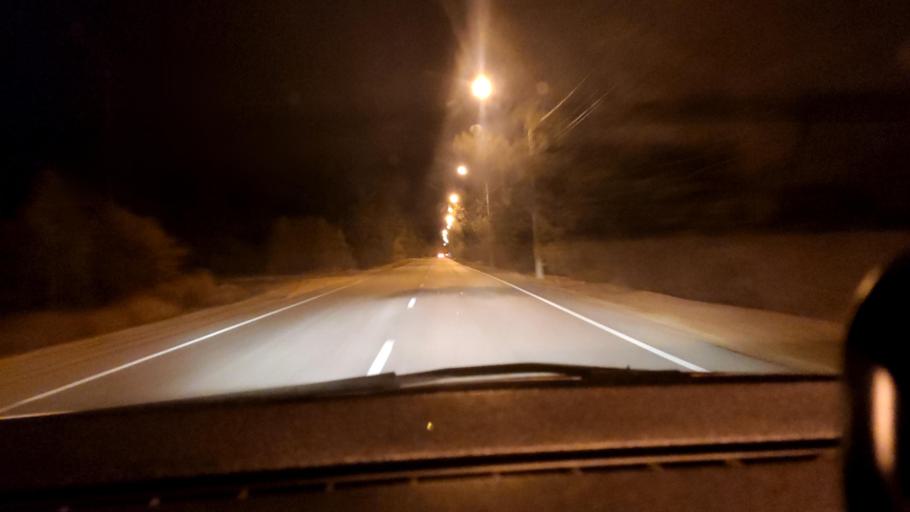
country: RU
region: Voronezj
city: Shilovo
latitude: 51.6088
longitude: 39.0454
